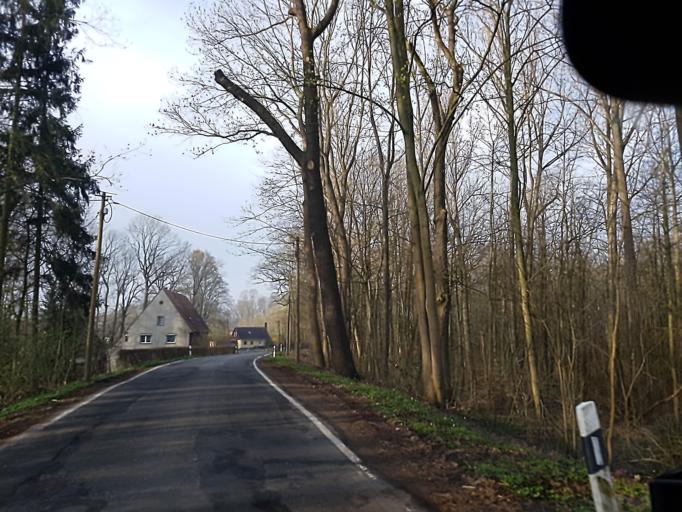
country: DE
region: Saxony
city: Stauchitz
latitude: 51.2632
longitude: 13.1872
